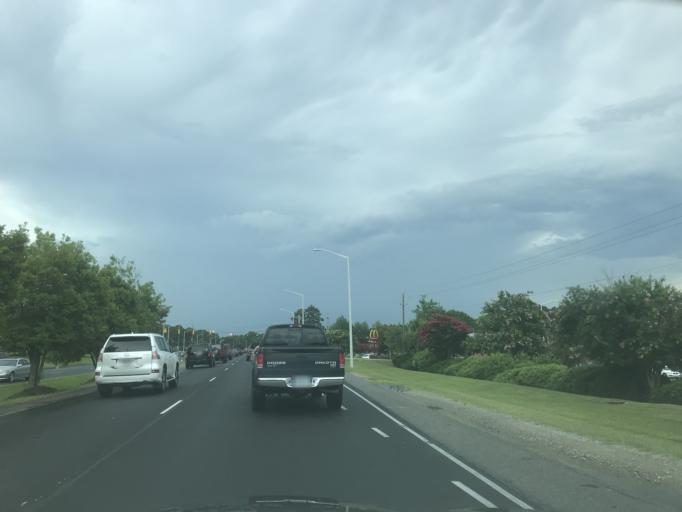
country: US
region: North Carolina
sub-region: Johnston County
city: Clayton
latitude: 35.6515
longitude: -78.4711
